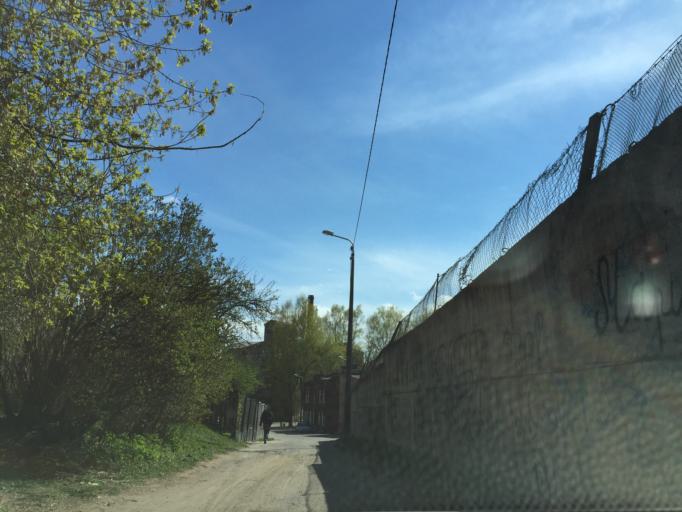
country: LV
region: Riga
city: Riga
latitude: 56.9271
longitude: 24.0959
